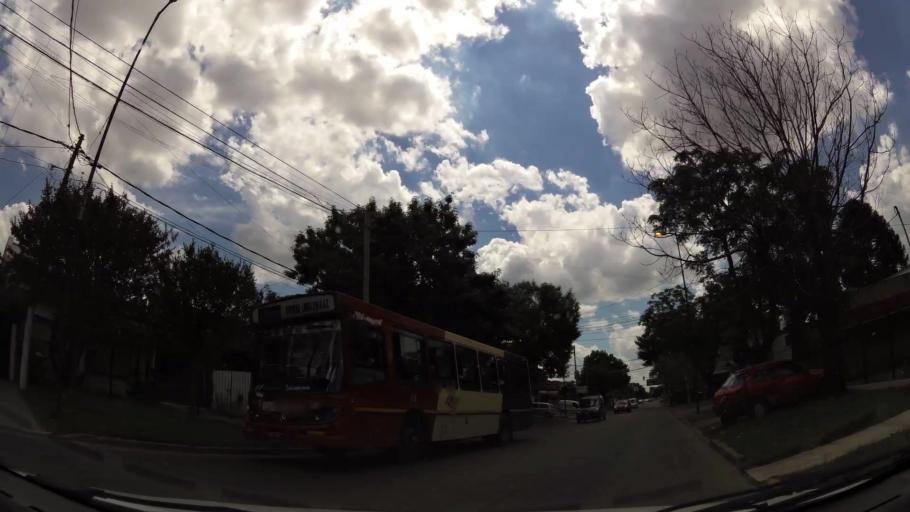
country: AR
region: Buenos Aires
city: Ituzaingo
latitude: -34.6557
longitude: -58.6774
